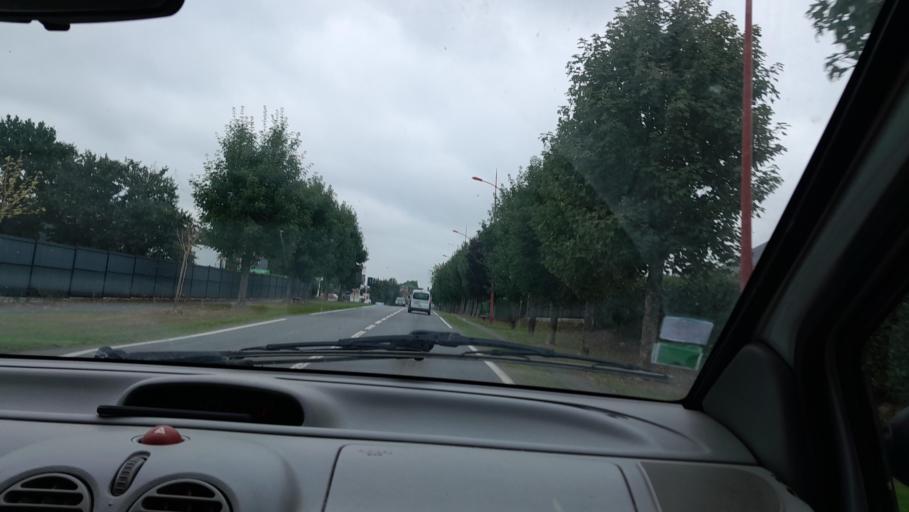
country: FR
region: Pays de la Loire
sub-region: Departement de la Mayenne
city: Cosse-le-Vivien
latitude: 47.9377
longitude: -0.9149
